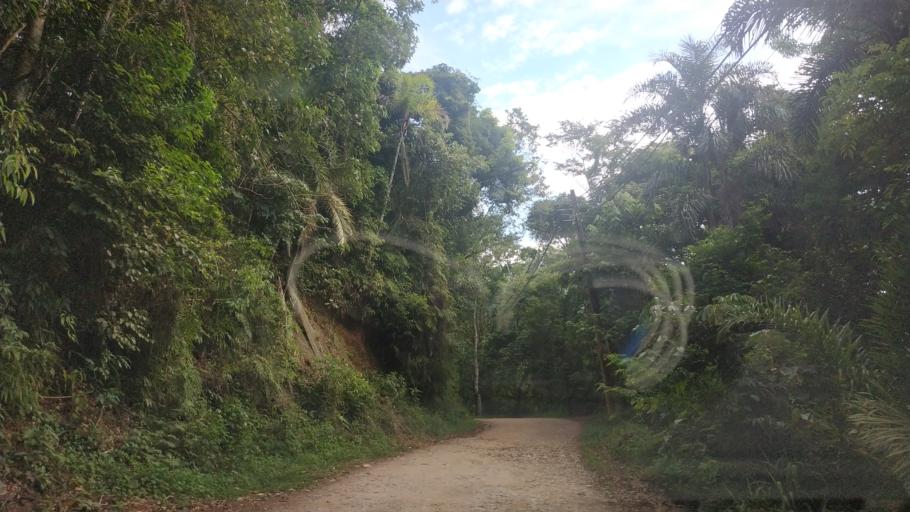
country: BR
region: Sao Paulo
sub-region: Ilhabela
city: Ilhabela
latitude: -23.8346
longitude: -45.3585
